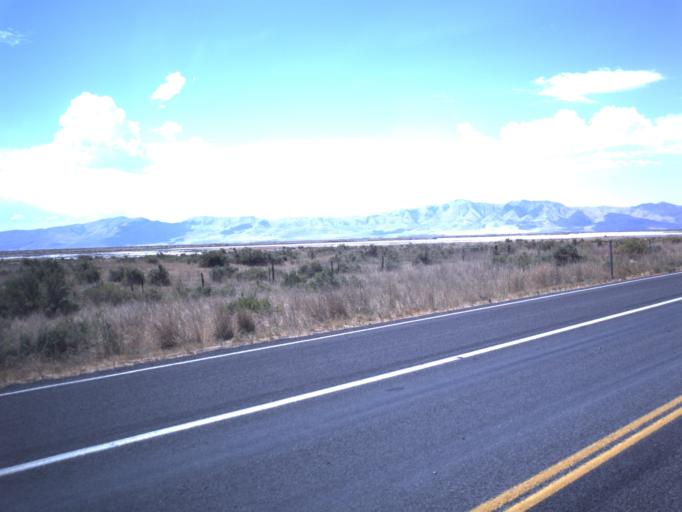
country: US
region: Utah
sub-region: Box Elder County
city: Elwood
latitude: 41.5790
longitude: -112.2474
